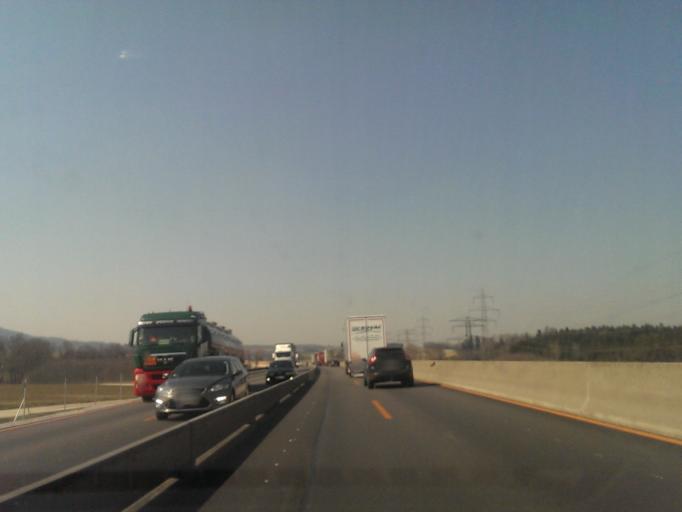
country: AT
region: Upper Austria
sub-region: Politischer Bezirk Vocklabruck
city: Wolfsegg am Hausruck
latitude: 48.1876
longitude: 13.6814
